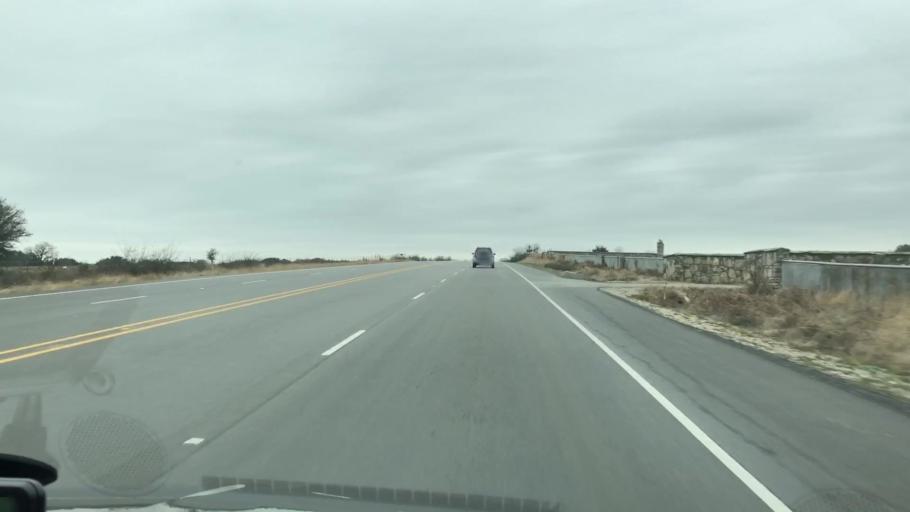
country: US
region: Texas
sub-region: Hamilton County
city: Hico
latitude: 32.0041
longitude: -98.0547
